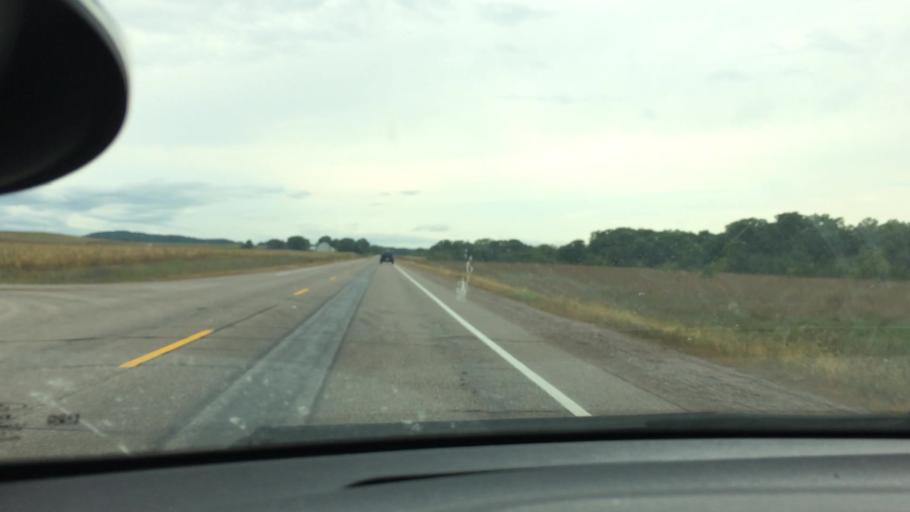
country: US
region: Wisconsin
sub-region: Eau Claire County
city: Augusta
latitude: 44.5858
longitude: -91.1294
